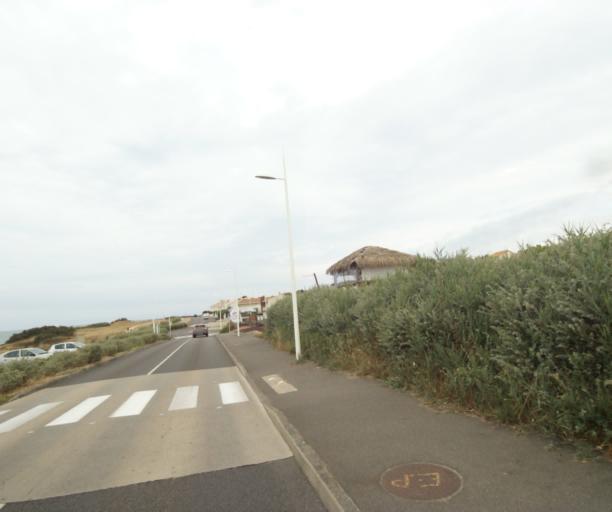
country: FR
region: Pays de la Loire
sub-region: Departement de la Vendee
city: Chateau-d'Olonne
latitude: 46.4747
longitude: -1.7526
